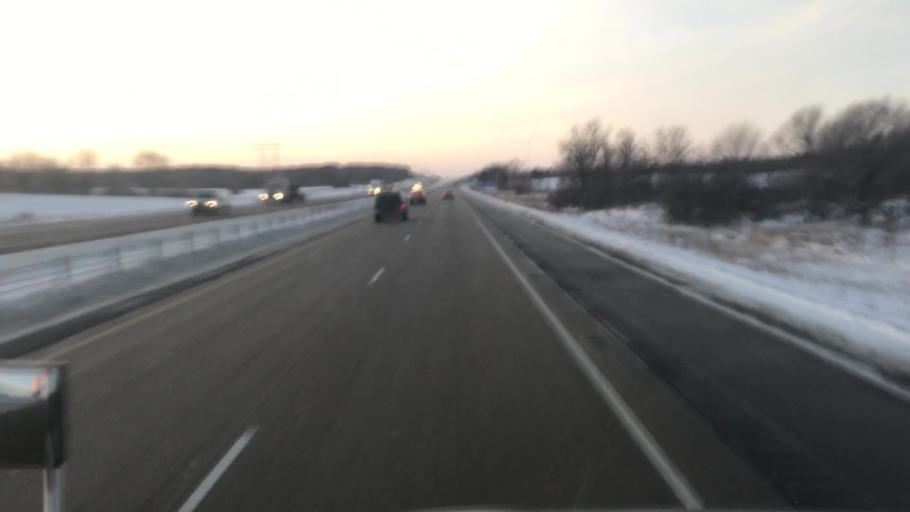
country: US
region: Minnesota
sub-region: Scott County
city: Elko New Market
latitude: 44.4824
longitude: -93.2921
